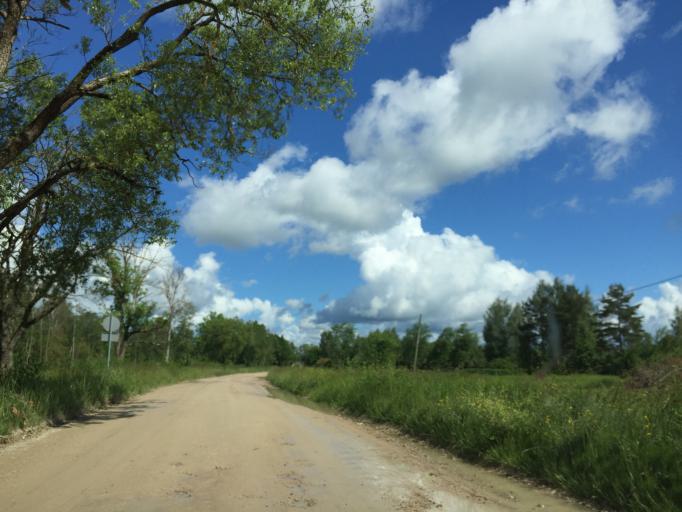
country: LV
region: Lecava
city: Iecava
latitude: 56.6161
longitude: 24.1885
